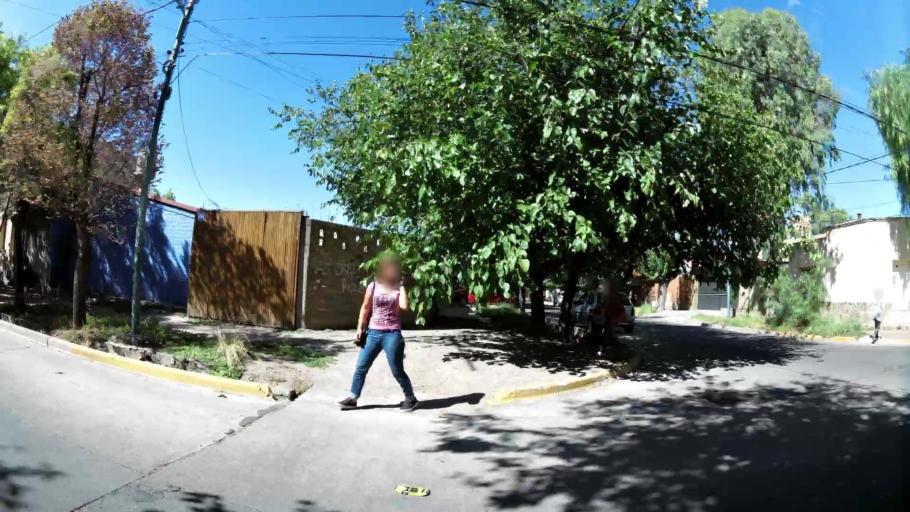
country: AR
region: Mendoza
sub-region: Departamento de Godoy Cruz
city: Godoy Cruz
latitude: -32.9066
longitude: -68.8595
